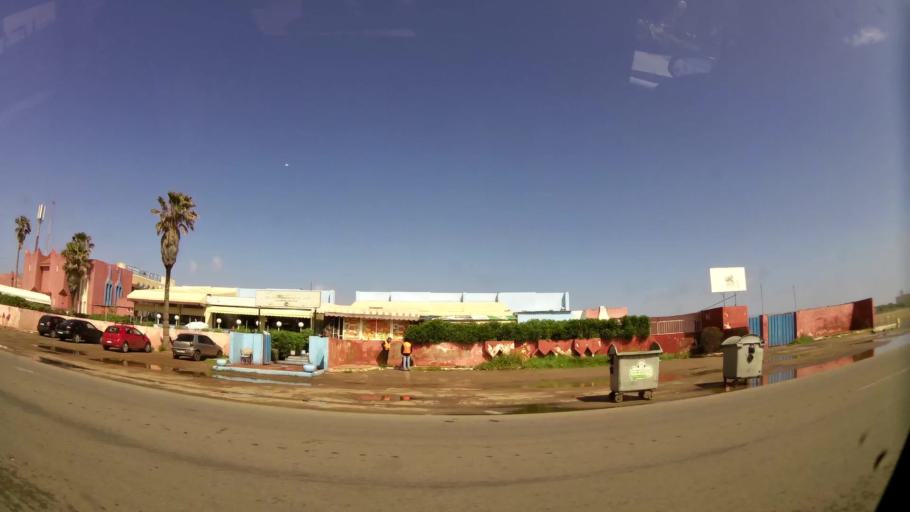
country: MA
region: Grand Casablanca
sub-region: Mediouna
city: Tit Mellil
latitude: 33.6233
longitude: -7.5257
